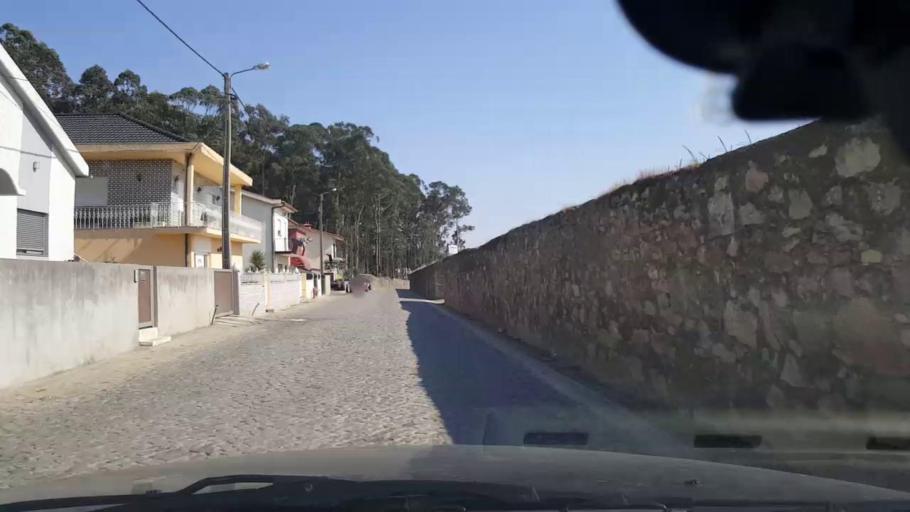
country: PT
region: Porto
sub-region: Povoa de Varzim
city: Pedroso
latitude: 41.4045
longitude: -8.6891
